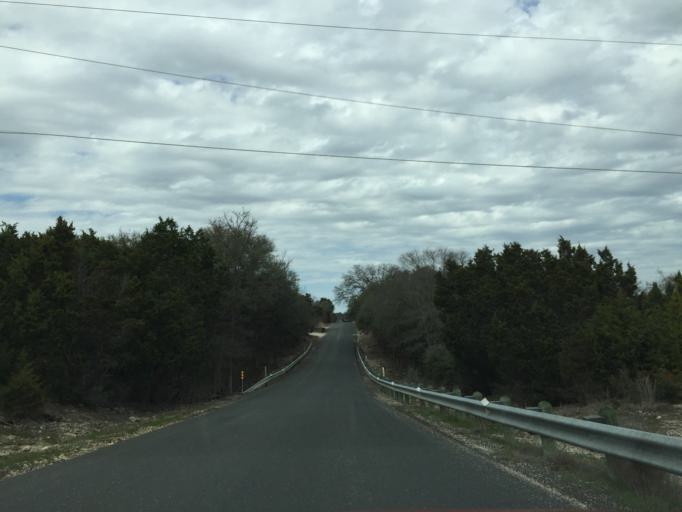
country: US
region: Texas
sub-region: Burnet County
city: Bertram
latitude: 30.7310
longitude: -97.9349
